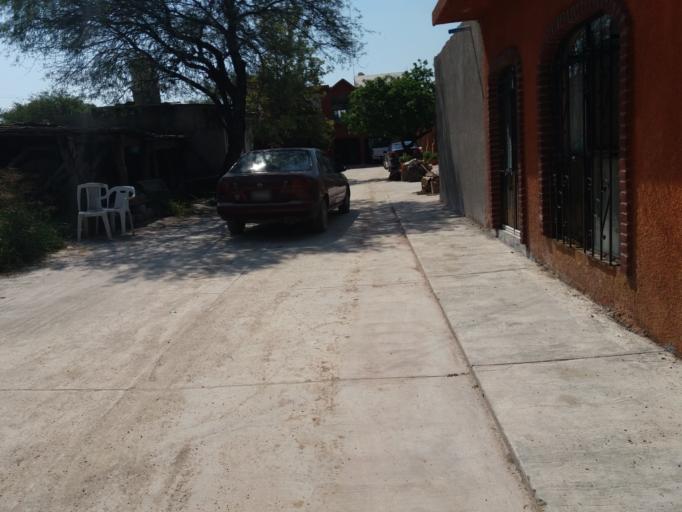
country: MX
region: Aguascalientes
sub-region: Aguascalientes
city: Penuelas (El Cienegal)
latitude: 21.7569
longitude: -102.2665
